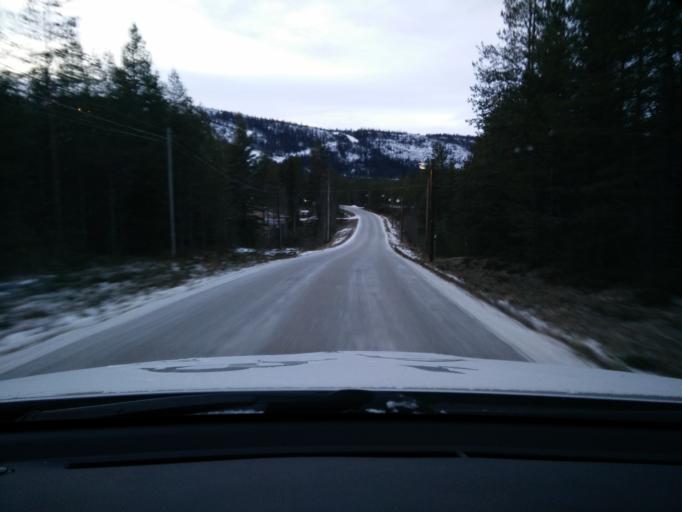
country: SE
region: Jaemtland
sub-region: Bergs Kommun
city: Hoverberg
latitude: 62.5048
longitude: 14.1943
